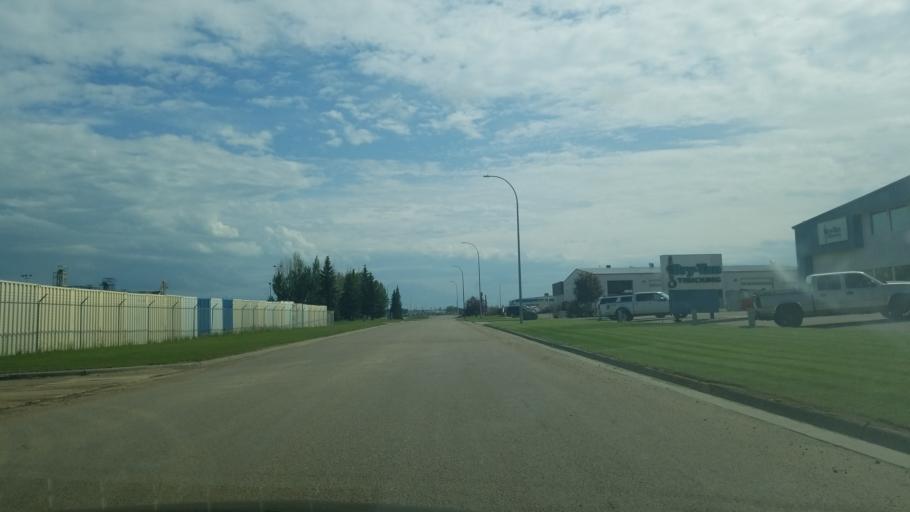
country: CA
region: Saskatchewan
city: Lloydminster
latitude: 53.2890
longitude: -110.0367
